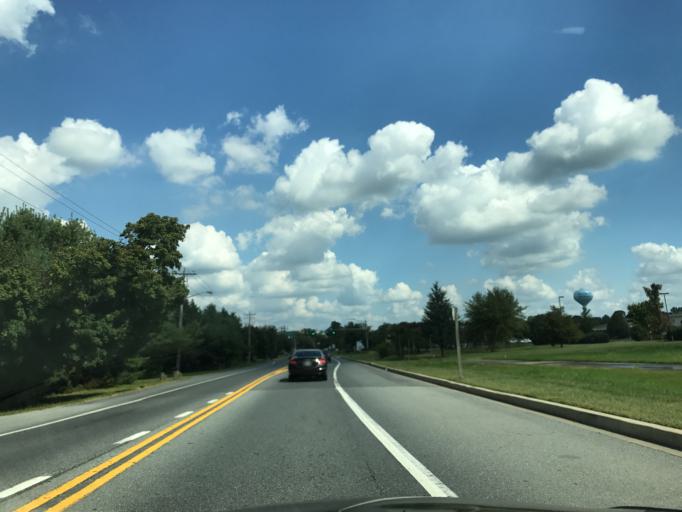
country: US
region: Maryland
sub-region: Queen Anne's County
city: Centreville
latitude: 39.0325
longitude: -76.0765
